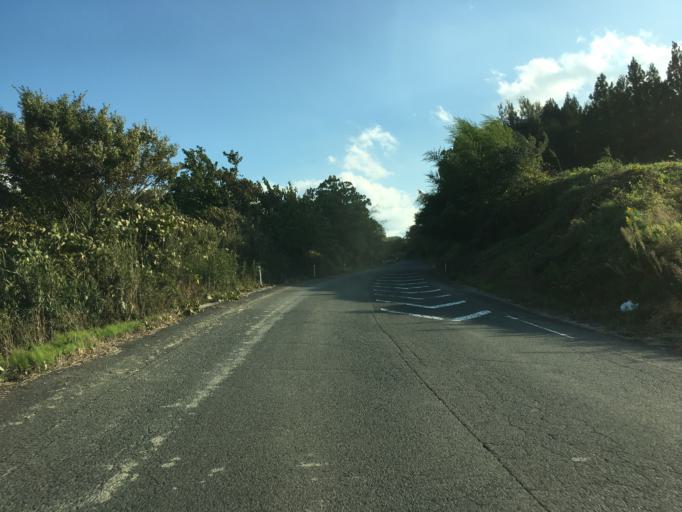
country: JP
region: Fukushima
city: Fukushima-shi
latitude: 37.6550
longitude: 140.5448
